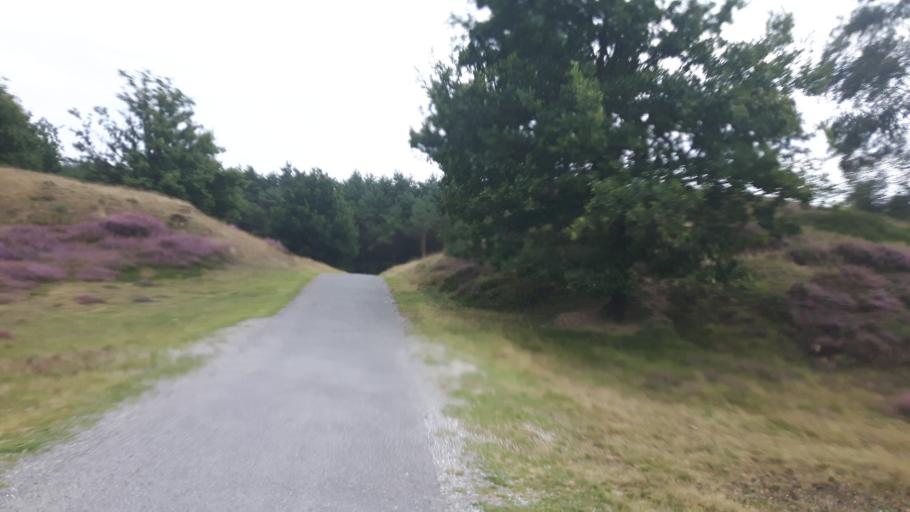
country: NL
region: Drenthe
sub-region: Gemeente Westerveld
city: Dwingeloo
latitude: 52.9341
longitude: 6.3131
